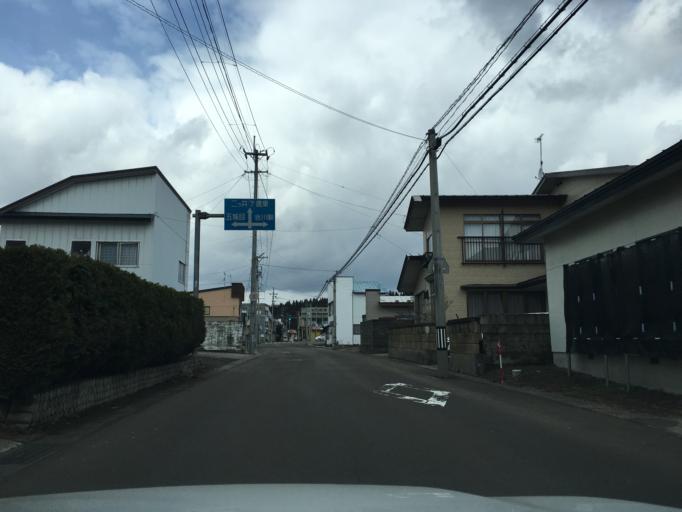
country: JP
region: Akita
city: Takanosu
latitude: 40.1601
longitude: 140.3312
